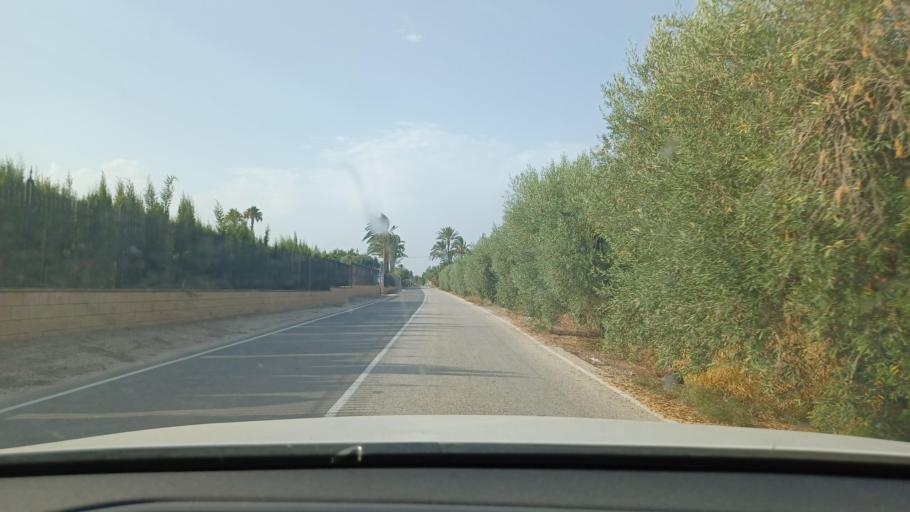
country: ES
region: Valencia
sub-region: Provincia de Alicante
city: Elche
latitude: 38.2302
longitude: -0.6939
